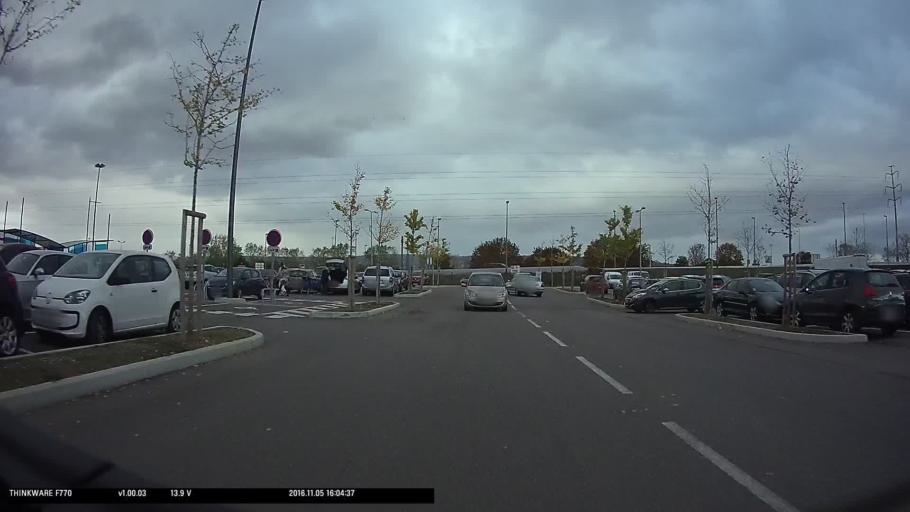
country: FR
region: Ile-de-France
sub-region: Departement des Yvelines
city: Flins-sur-Seine
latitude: 48.9672
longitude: 1.8638
